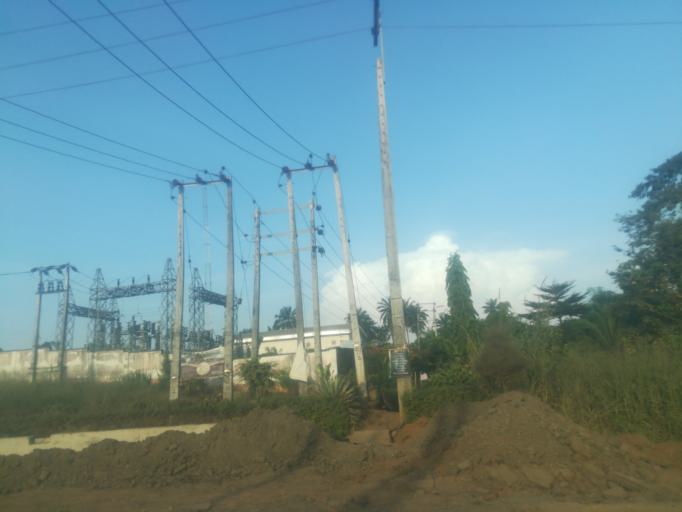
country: NG
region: Oyo
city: Moniya
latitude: 7.5447
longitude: 3.8964
